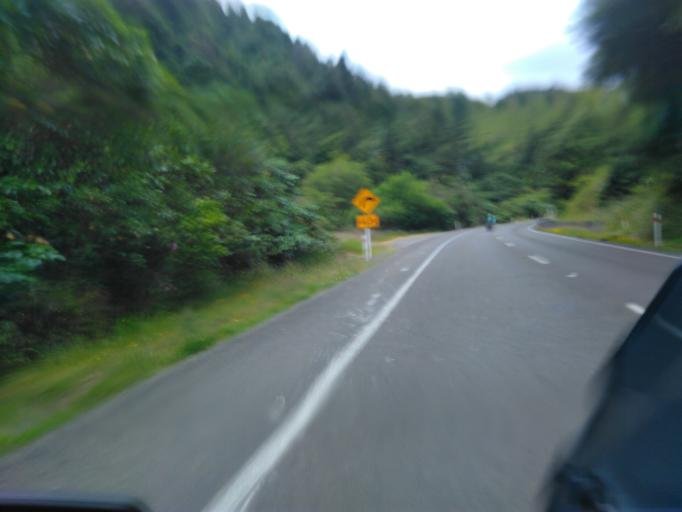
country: NZ
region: Bay of Plenty
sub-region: Opotiki District
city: Opotiki
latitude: -38.3399
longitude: 177.4340
